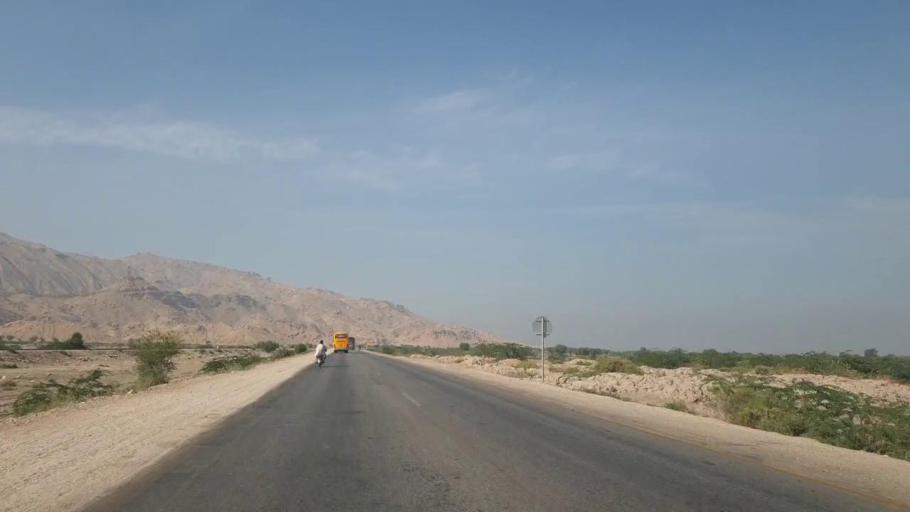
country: PK
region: Sindh
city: Sehwan
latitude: 26.2773
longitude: 67.8980
